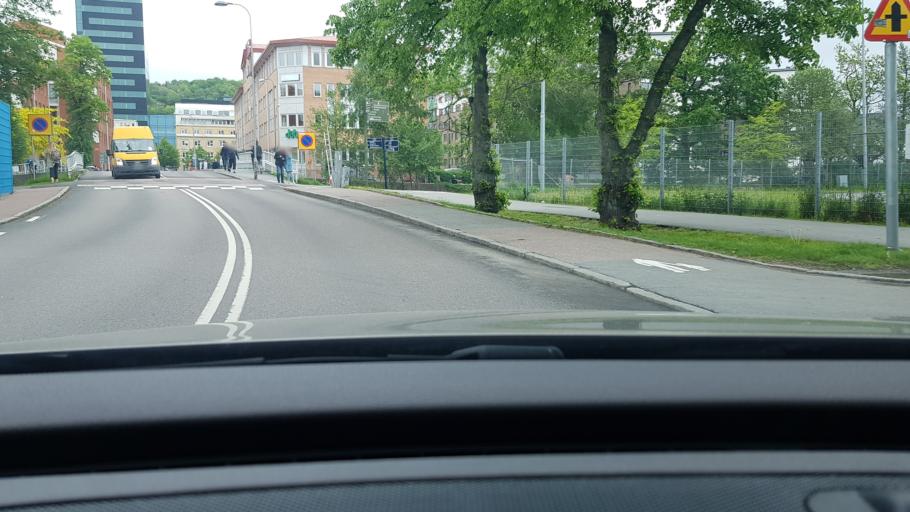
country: SE
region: Vaestra Goetaland
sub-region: Goteborg
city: Goeteborg
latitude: 57.7044
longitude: 11.9895
